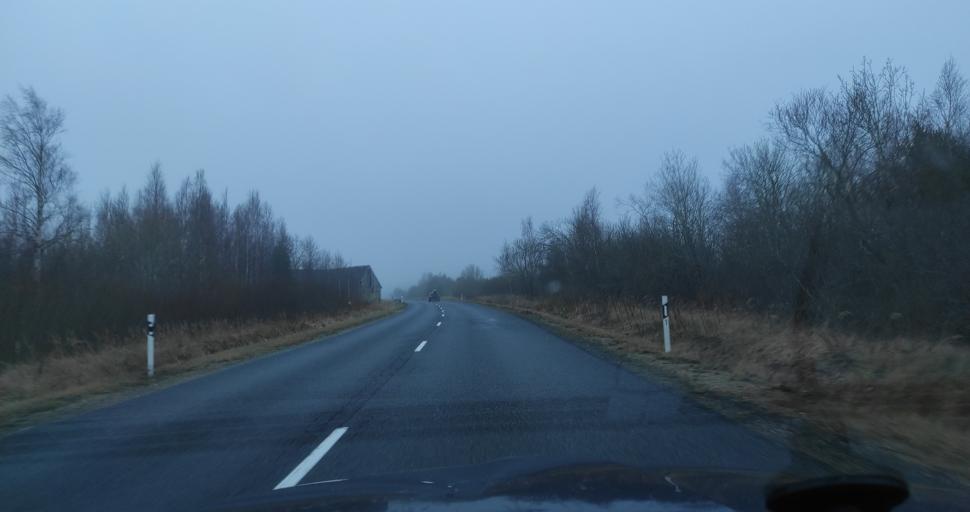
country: LV
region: Alsunga
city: Alsunga
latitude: 57.1143
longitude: 21.4231
